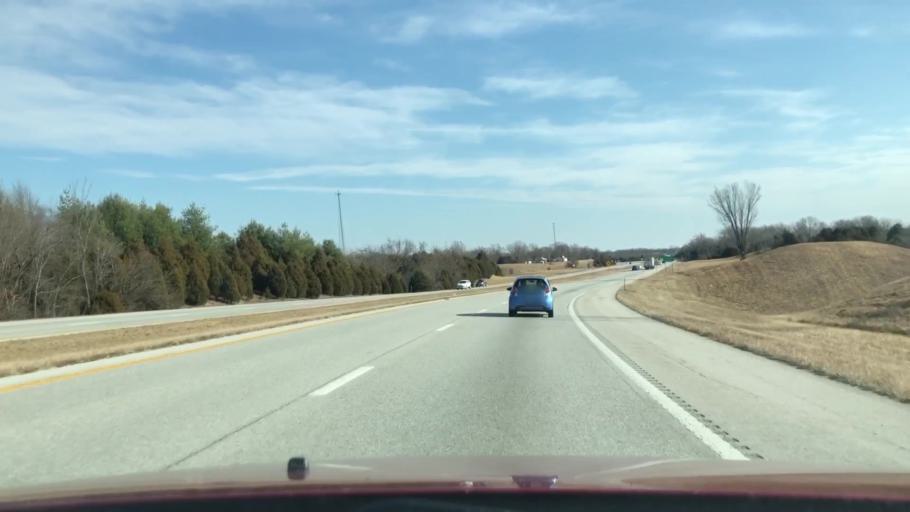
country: US
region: Missouri
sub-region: Webster County
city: Rogersville
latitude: 37.1508
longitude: -92.9480
